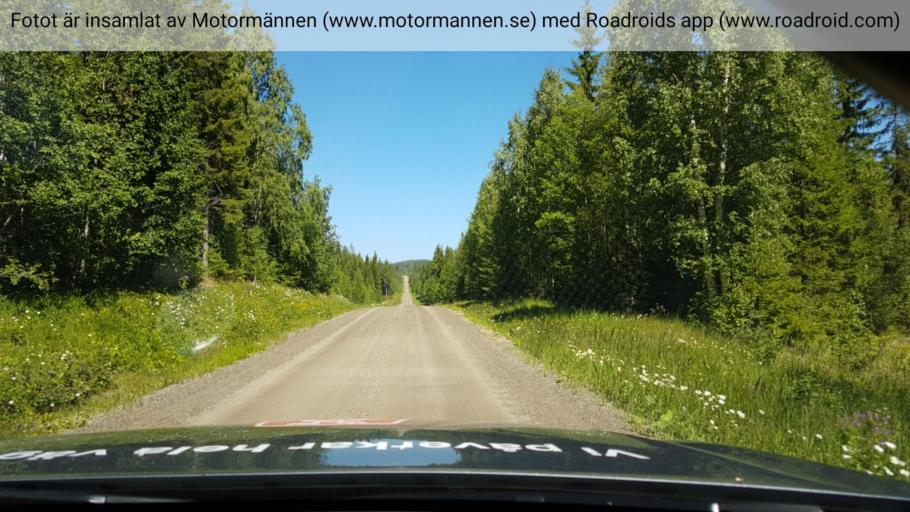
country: SE
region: Jaemtland
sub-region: Braecke Kommun
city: Braecke
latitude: 62.8092
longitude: 15.2248
